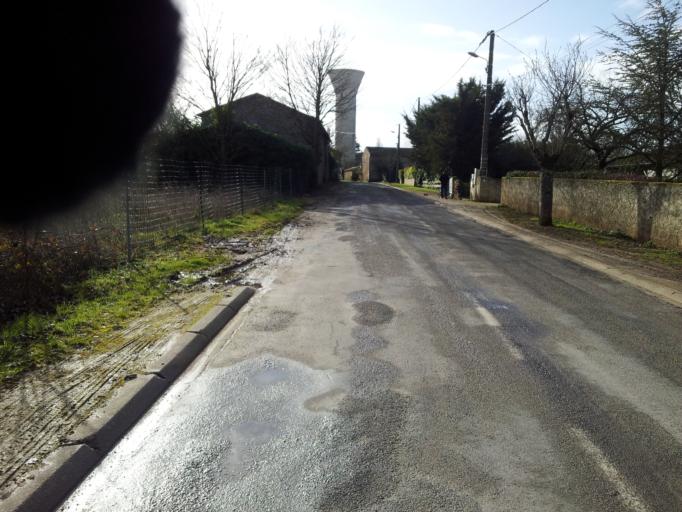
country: FR
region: Poitou-Charentes
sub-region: Departement de la Vienne
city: Avanton
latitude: 46.6604
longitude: 0.3279
